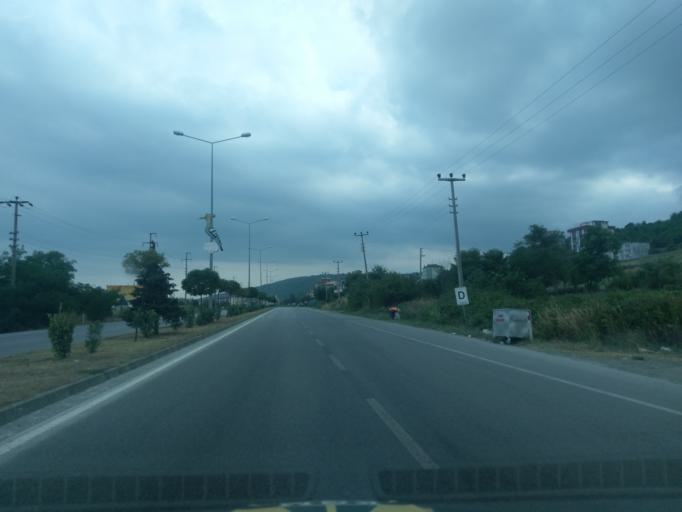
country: TR
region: Samsun
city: Taflan
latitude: 41.4123
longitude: 36.1753
